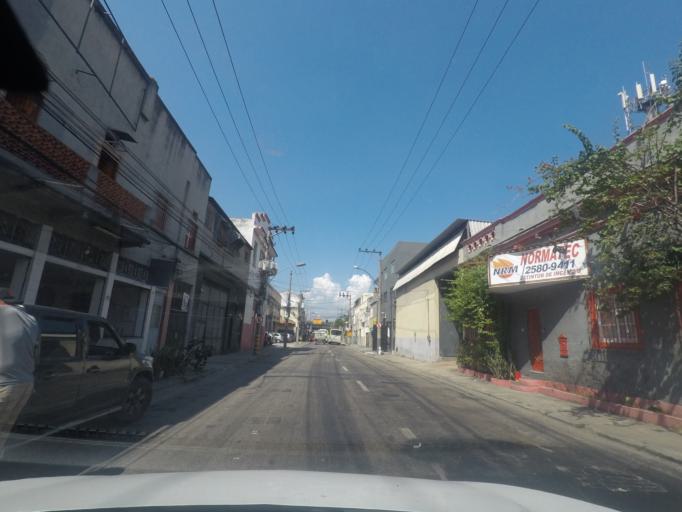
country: BR
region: Rio de Janeiro
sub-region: Rio De Janeiro
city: Rio de Janeiro
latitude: -22.8913
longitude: -43.2201
